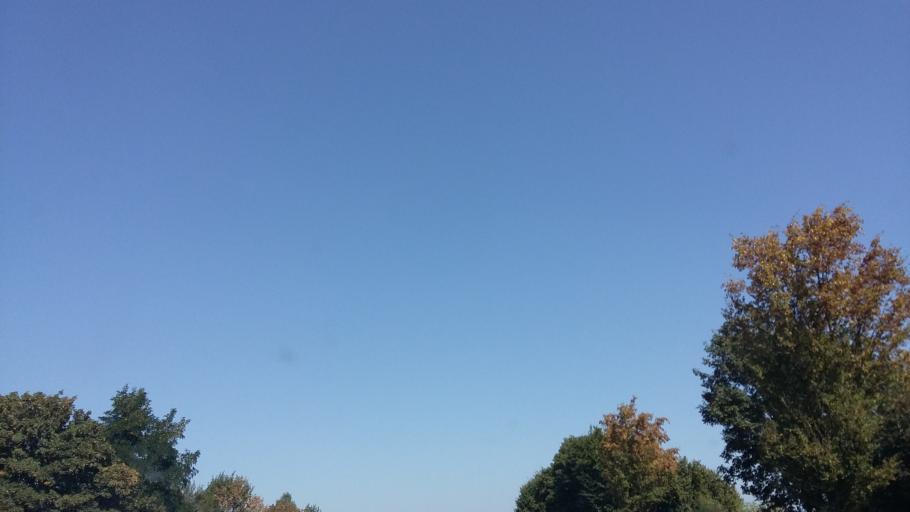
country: DE
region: Bavaria
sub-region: Swabia
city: Oberottmarshausen
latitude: 48.2115
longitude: 10.8596
